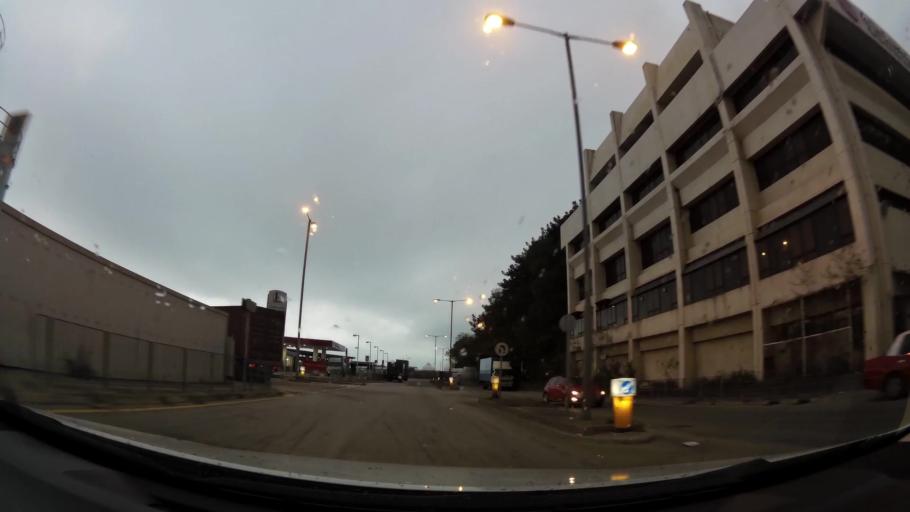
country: HK
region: Tsuen Wan
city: Tsuen Wan
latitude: 22.3307
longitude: 114.1063
